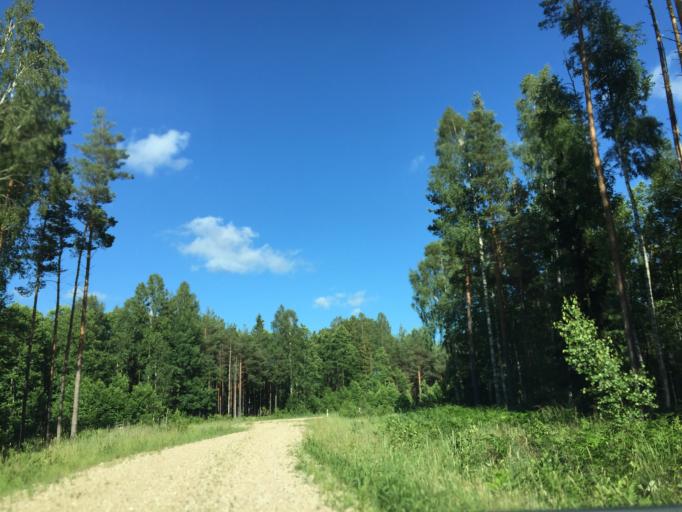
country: LV
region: Ventspils
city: Ventspils
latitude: 57.5397
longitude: 21.7399
